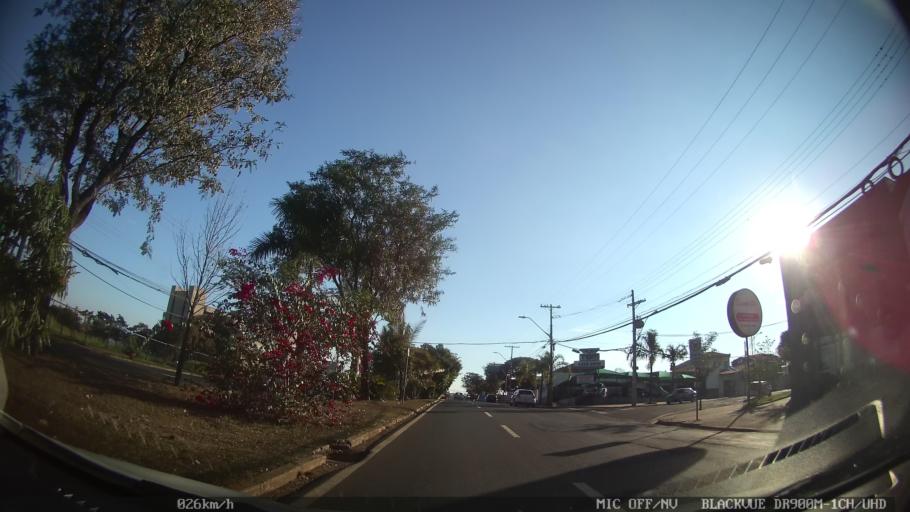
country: BR
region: Sao Paulo
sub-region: Piracicaba
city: Piracicaba
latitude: -22.7034
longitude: -47.6530
